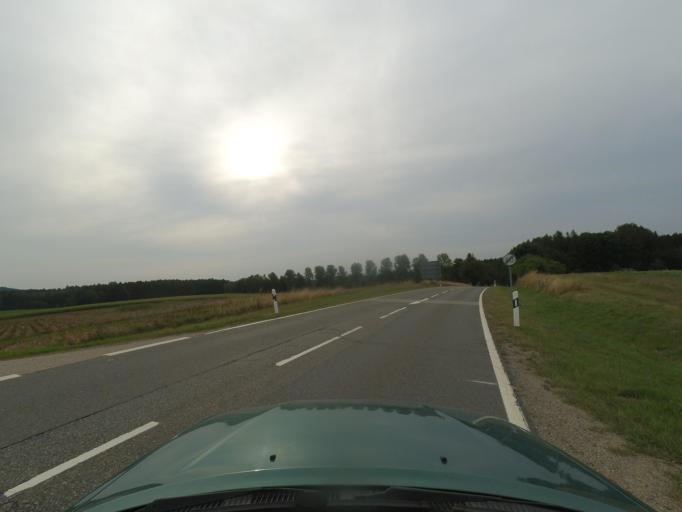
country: DE
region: Bavaria
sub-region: Upper Palatinate
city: Vohenstrauss
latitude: 49.6153
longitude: 12.3539
